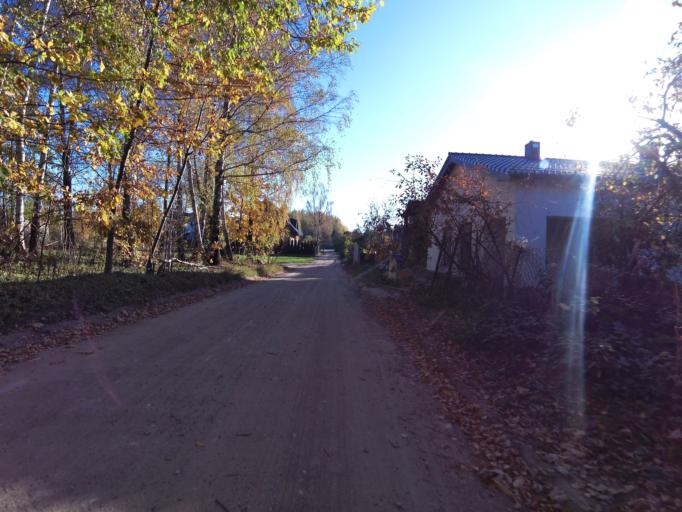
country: LT
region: Vilnius County
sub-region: Vilnius
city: Fabijoniskes
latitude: 54.7445
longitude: 25.2610
